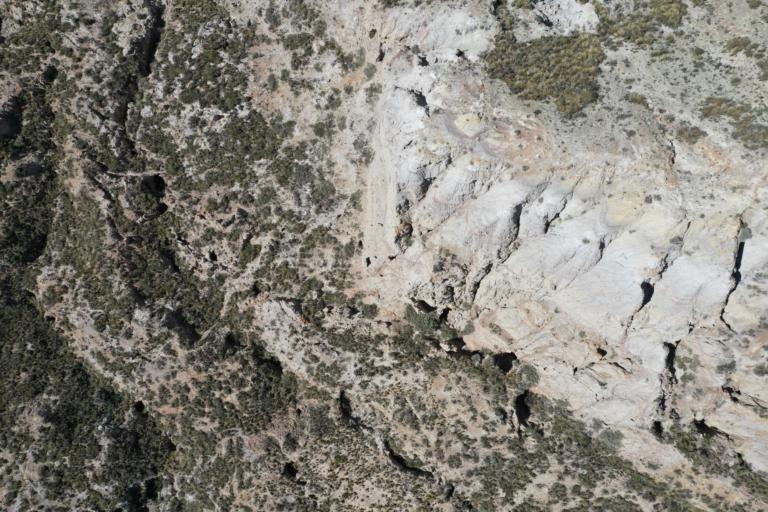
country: BO
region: La Paz
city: La Paz
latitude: -16.5577
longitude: -68.1219
